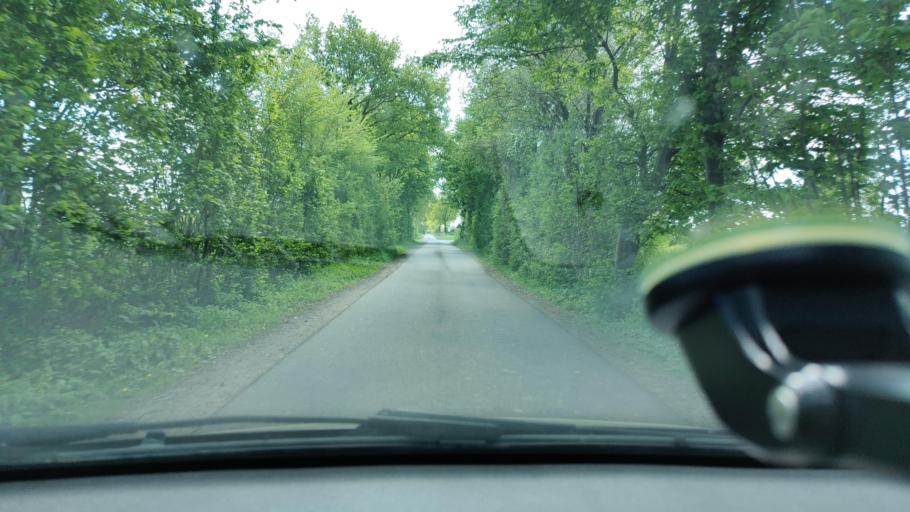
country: DE
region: North Rhine-Westphalia
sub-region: Regierungsbezirk Dusseldorf
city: Bocholt
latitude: 51.8276
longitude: 6.5532
